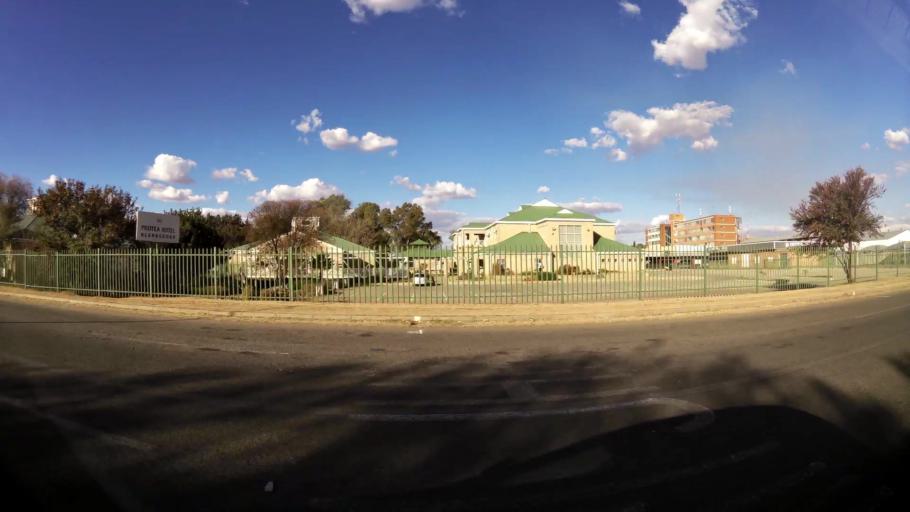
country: ZA
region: North-West
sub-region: Dr Kenneth Kaunda District Municipality
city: Klerksdorp
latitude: -26.8618
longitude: 26.6691
